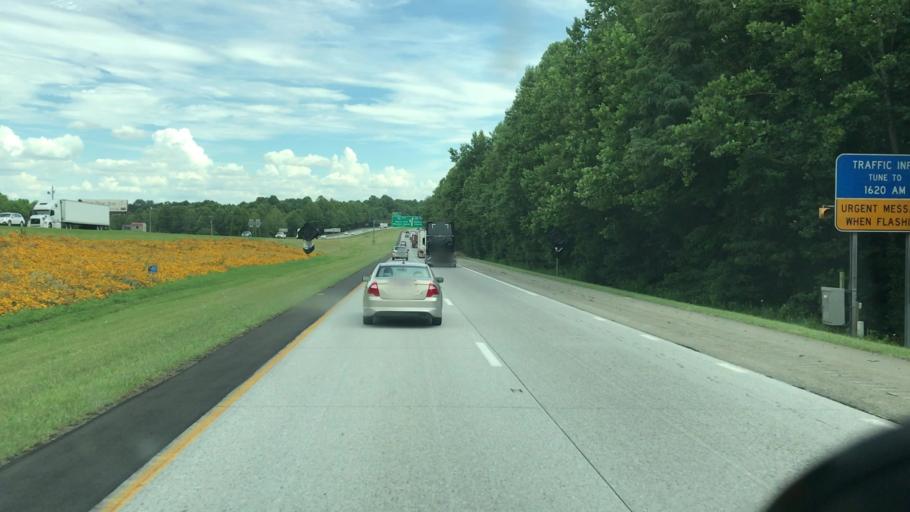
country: US
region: Virginia
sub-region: Carroll County
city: Cana
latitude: 36.5201
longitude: -80.7452
